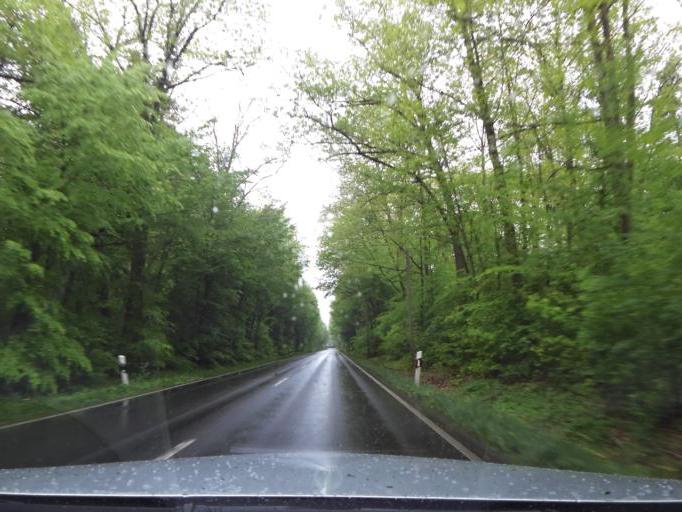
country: DE
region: Hesse
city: Morfelden-Walldorf
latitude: 49.9538
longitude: 8.5791
